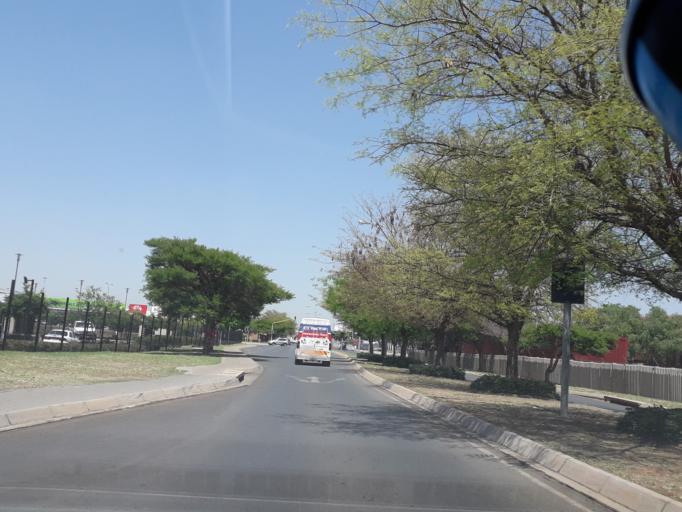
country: ZA
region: Gauteng
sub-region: City of Tshwane Metropolitan Municipality
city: Centurion
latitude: -25.8743
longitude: 28.1661
